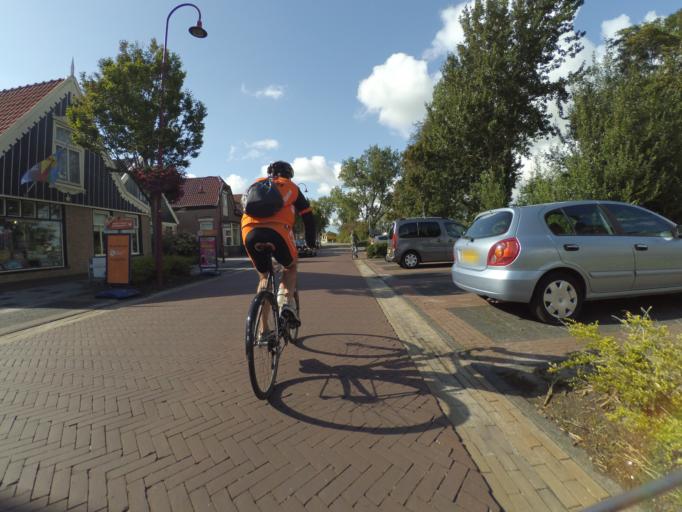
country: NL
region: North Holland
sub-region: Gemeente Schagen
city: Schagen
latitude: 52.8367
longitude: 4.7549
